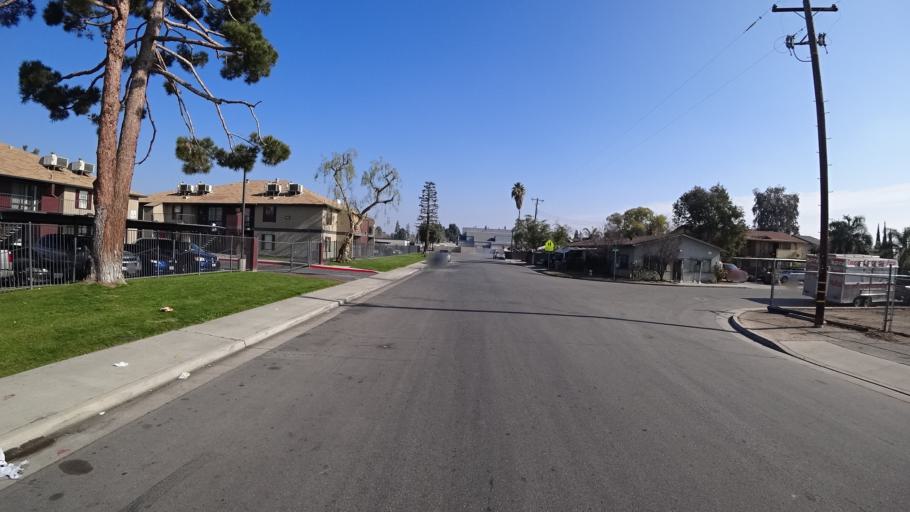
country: US
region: California
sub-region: Kern County
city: Bakersfield
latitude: 35.3944
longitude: -119.0156
